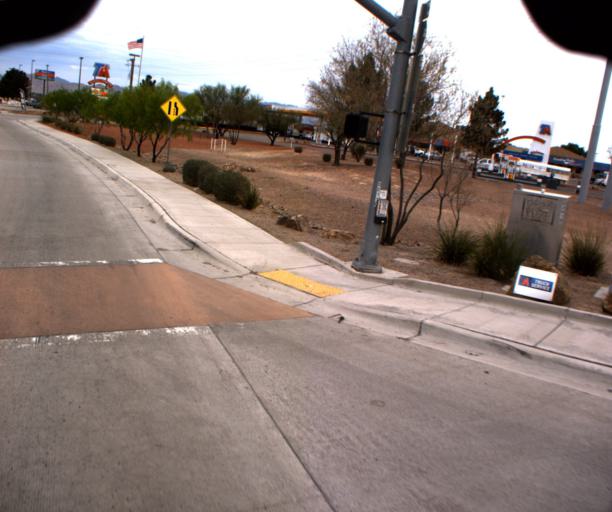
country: US
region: Arizona
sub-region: Cochise County
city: Willcox
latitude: 32.2678
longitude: -109.8467
